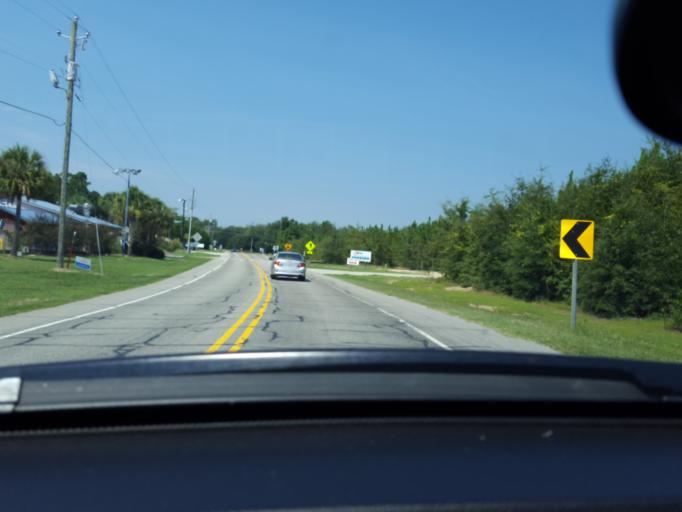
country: US
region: North Carolina
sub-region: Bladen County
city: Elizabethtown
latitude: 34.6481
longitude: -78.5195
